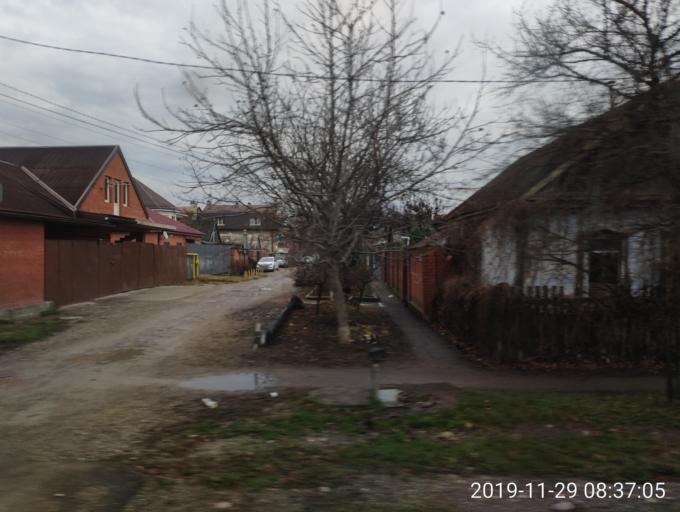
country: RU
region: Krasnodarskiy
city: Krasnodar
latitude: 45.0524
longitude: 39.0029
